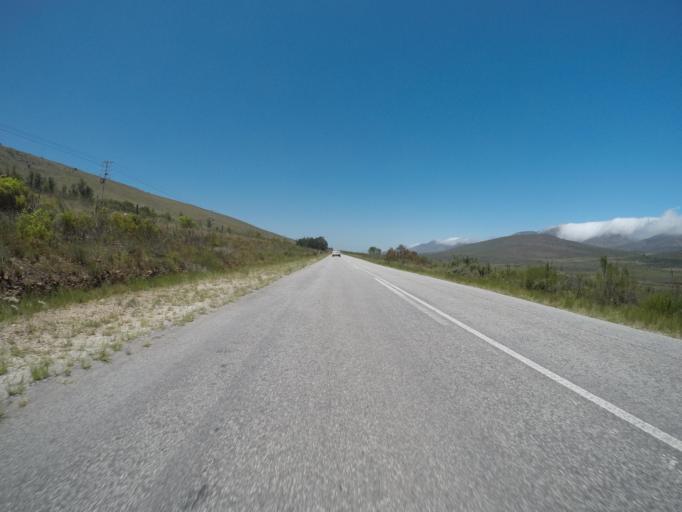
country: ZA
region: Eastern Cape
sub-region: Cacadu District Municipality
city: Kareedouw
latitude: -33.8435
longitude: 23.9434
